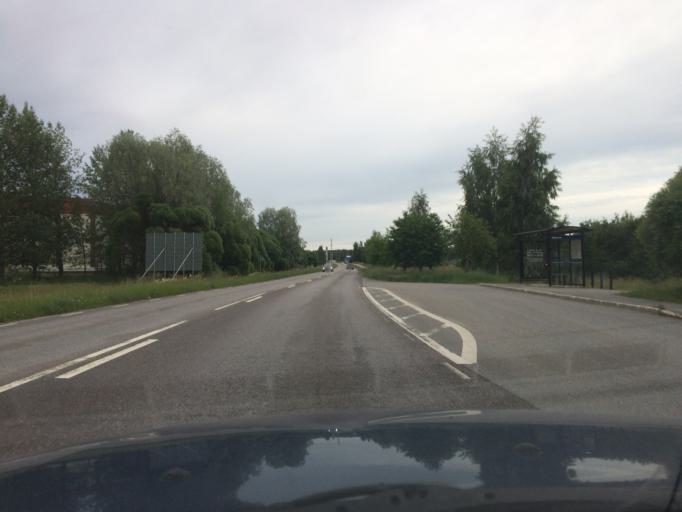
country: SE
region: Norrbotten
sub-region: Pitea Kommun
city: Bergsviken
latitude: 65.3452
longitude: 21.4056
